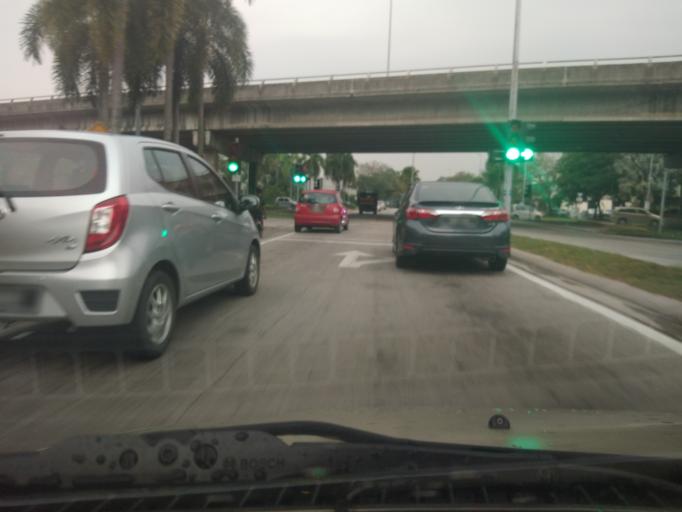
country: MY
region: Penang
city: Permatang Kuching
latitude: 5.4471
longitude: 100.3964
